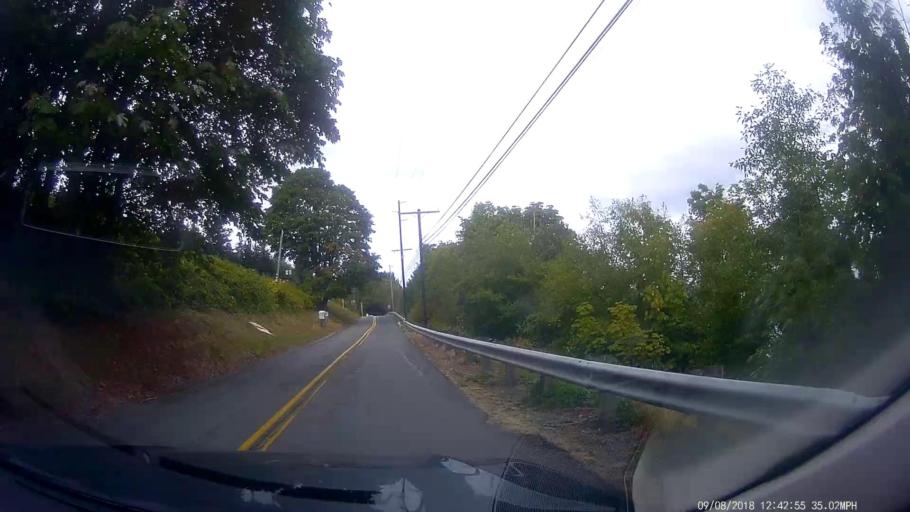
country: US
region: Washington
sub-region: Skagit County
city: Anacortes
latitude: 48.4867
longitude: -122.5979
